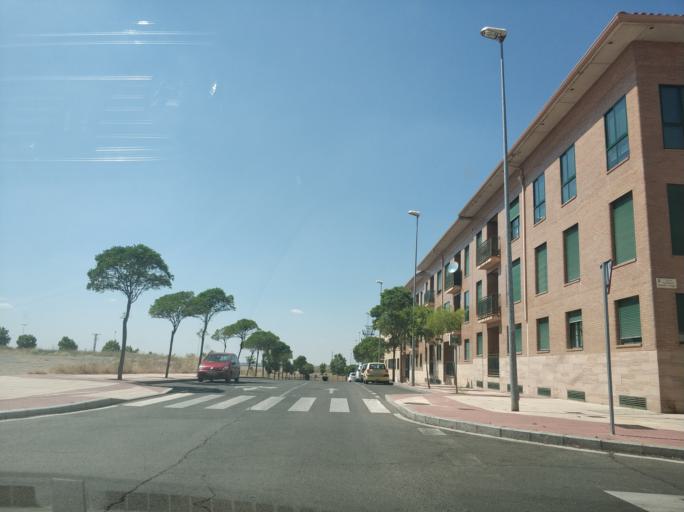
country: ES
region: Castille and Leon
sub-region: Provincia de Salamanca
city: Salamanca
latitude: 40.9761
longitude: -5.6821
